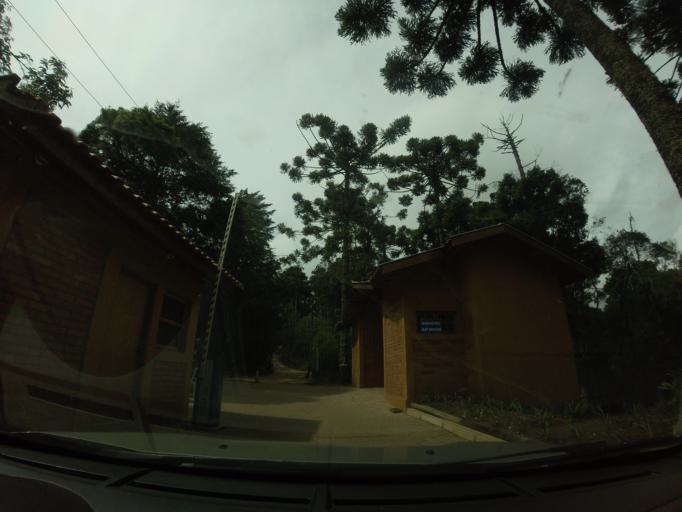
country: BR
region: Sao Paulo
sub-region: Campos Do Jordao
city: Campos do Jordao
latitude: -22.6786
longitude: -45.6485
